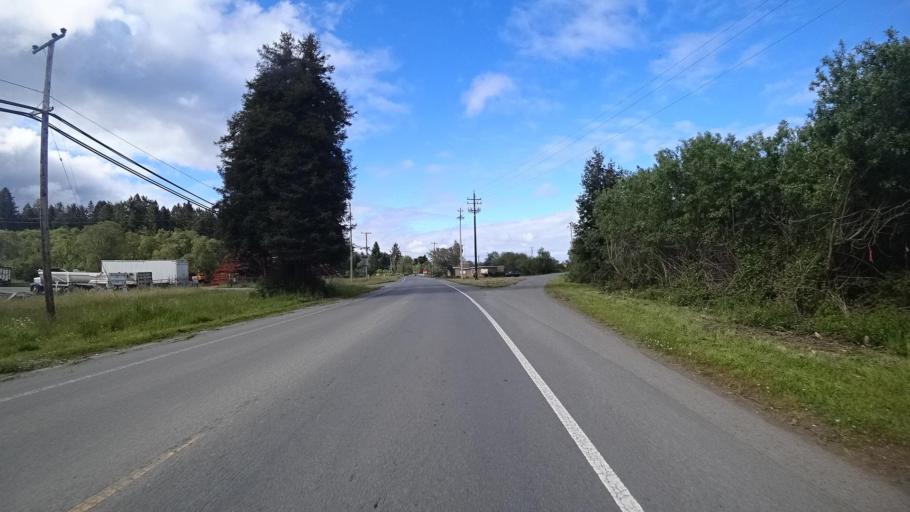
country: US
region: California
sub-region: Humboldt County
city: Arcata
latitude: 40.8951
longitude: -124.0779
